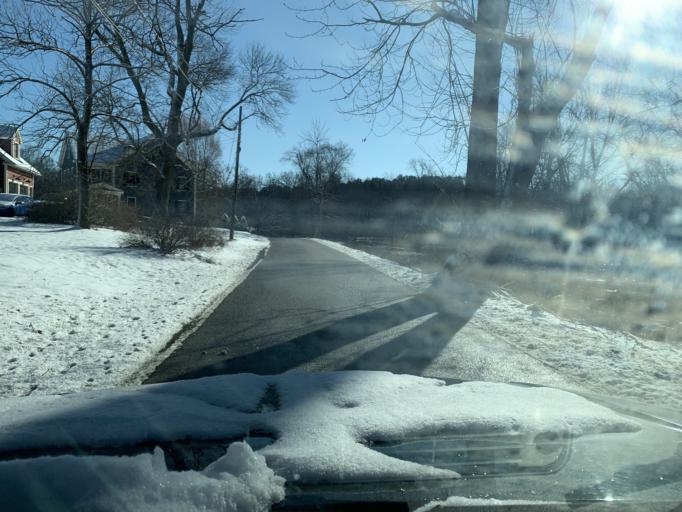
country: US
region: Massachusetts
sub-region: Essex County
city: Topsfield
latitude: 42.6280
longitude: -70.9508
